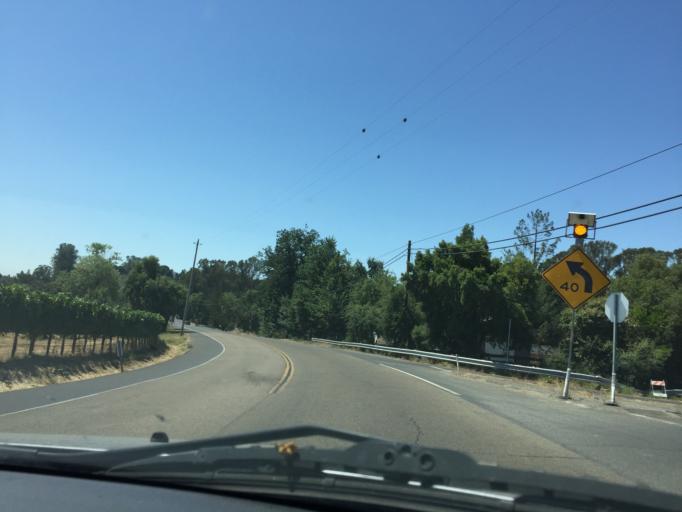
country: US
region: California
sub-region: Napa County
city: Napa
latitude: 38.2846
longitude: -122.3234
